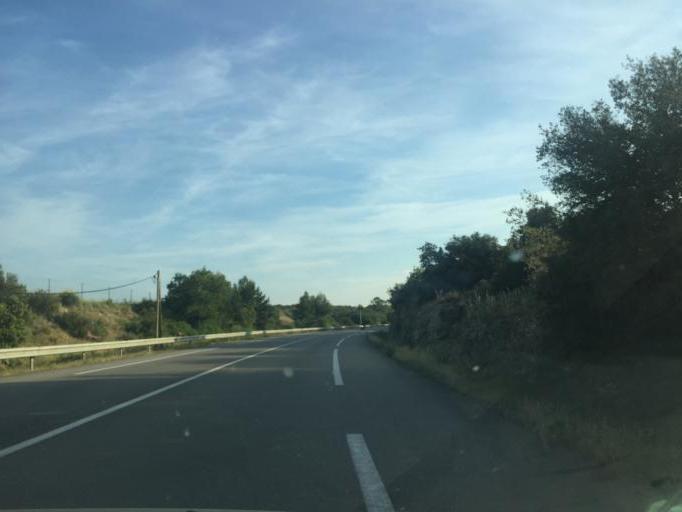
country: FR
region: Languedoc-Roussillon
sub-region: Departement du Gard
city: Pujaut
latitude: 44.0172
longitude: 4.7411
